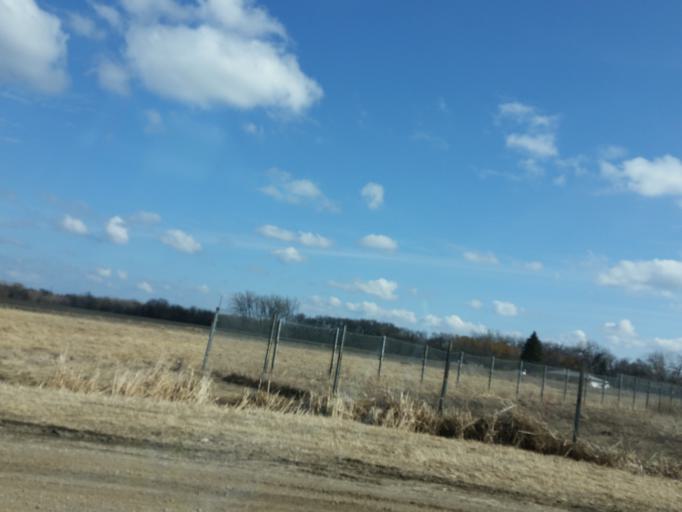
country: US
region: North Dakota
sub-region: Walsh County
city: Grafton
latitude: 48.4290
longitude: -97.4107
